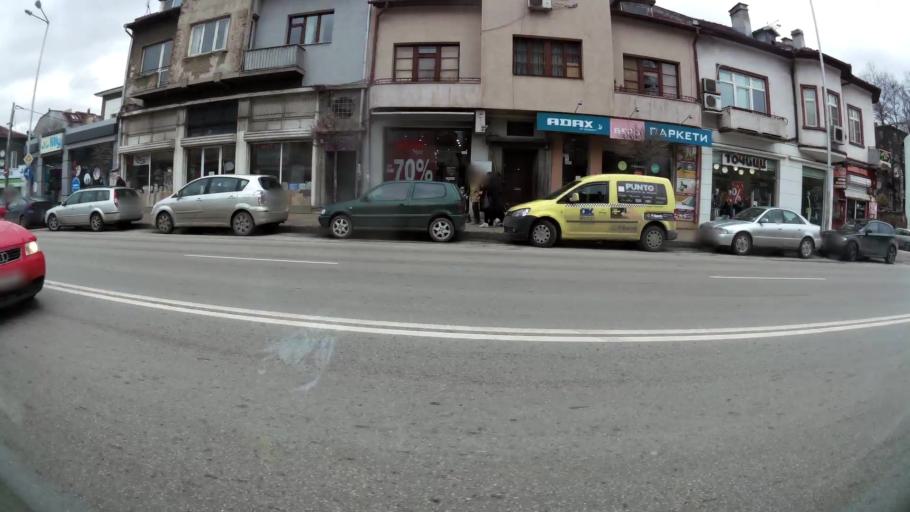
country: BG
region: Sofia-Capital
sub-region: Stolichna Obshtina
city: Sofia
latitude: 42.7253
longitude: 23.3038
